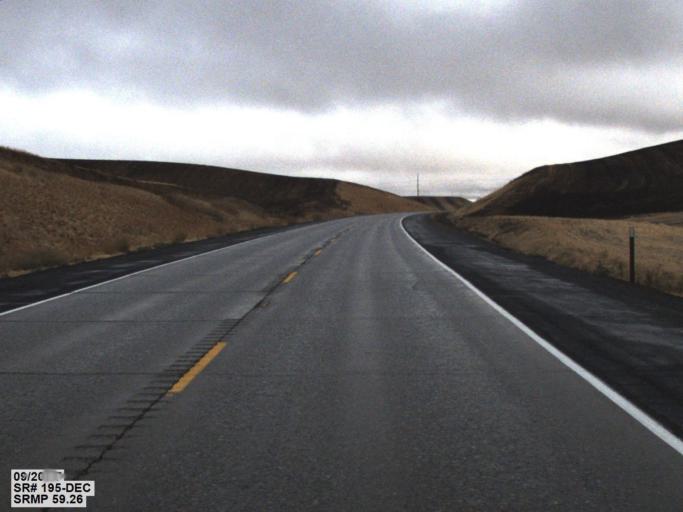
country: US
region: Washington
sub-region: Whitman County
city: Colfax
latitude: 47.1641
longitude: -117.3786
